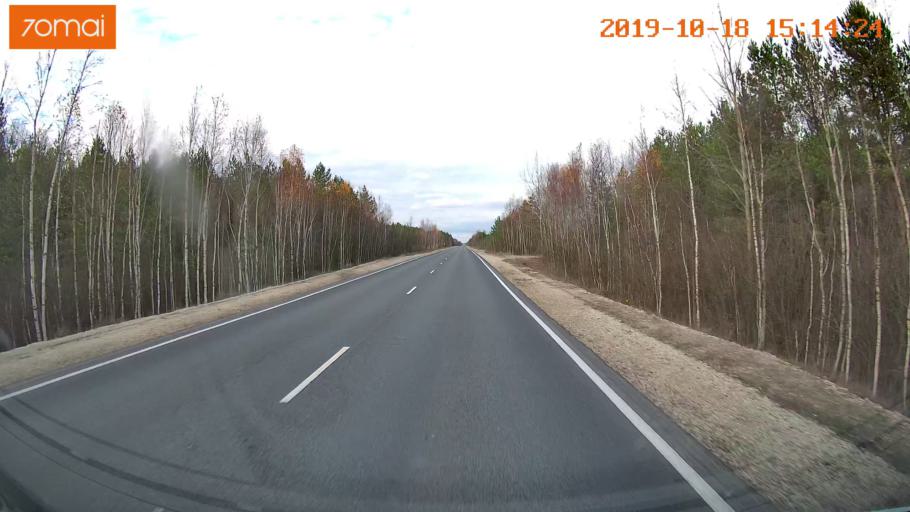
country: RU
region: Vladimir
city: Gus'-Khrustal'nyy
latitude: 55.6021
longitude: 40.7202
